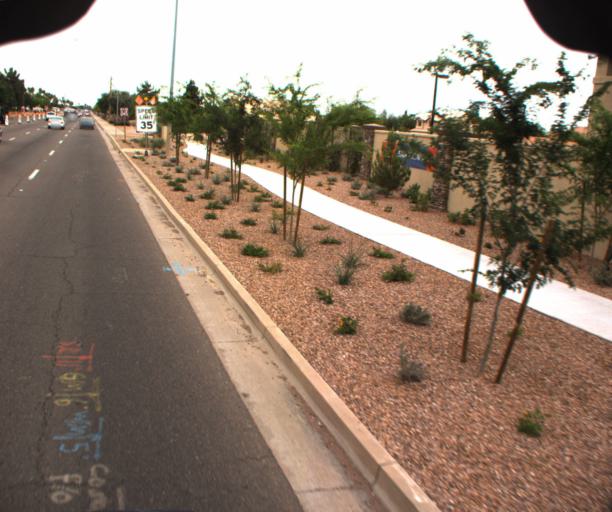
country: US
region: Arizona
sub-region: Maricopa County
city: San Carlos
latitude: 33.3720
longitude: -111.8423
